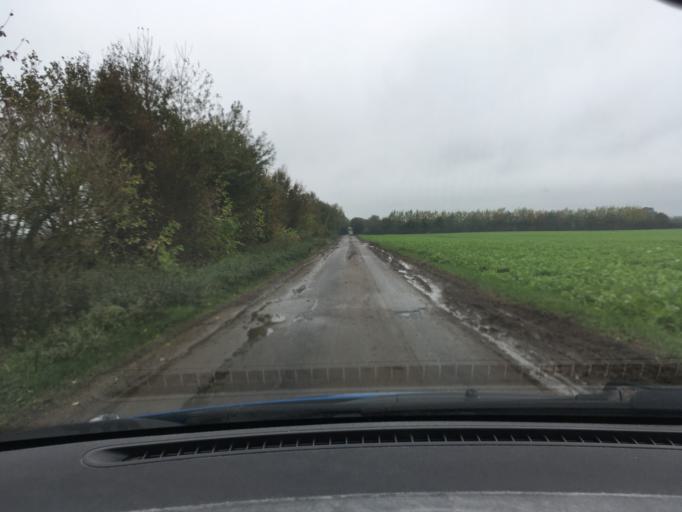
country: DE
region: Schleswig-Holstein
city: Bosau
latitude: 54.1027
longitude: 10.4714
